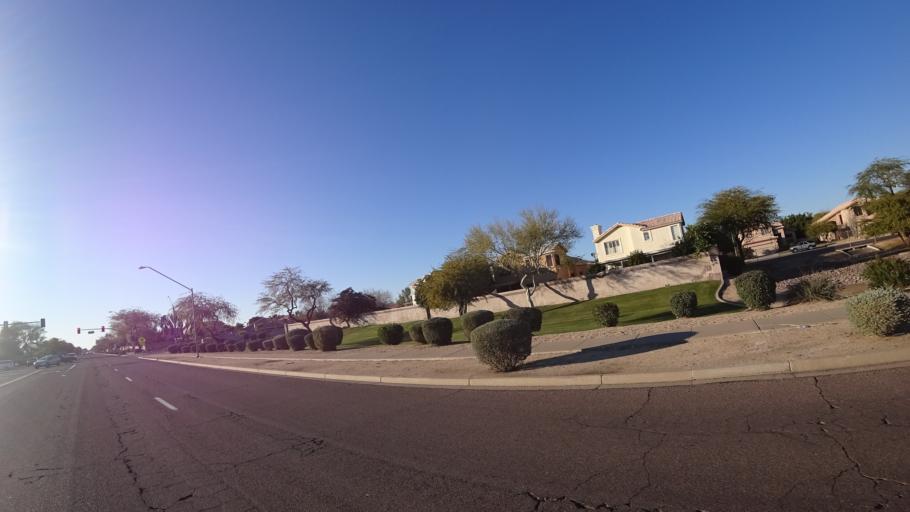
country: US
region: Arizona
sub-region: Maricopa County
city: Sun City
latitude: 33.6818
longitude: -112.2107
